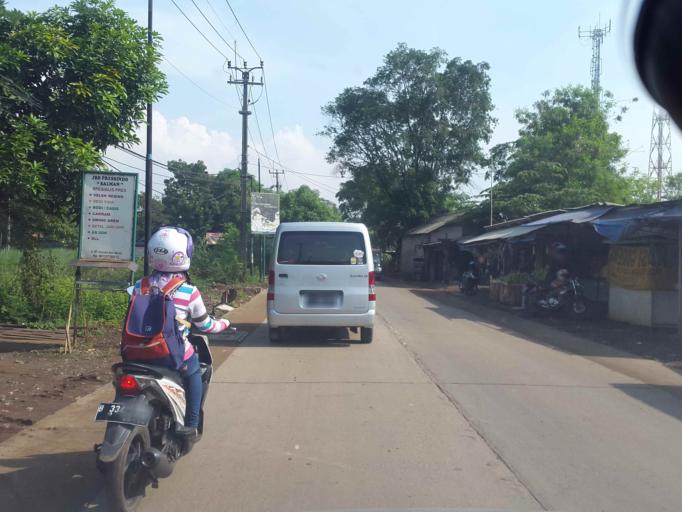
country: ID
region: West Java
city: Cileungsir
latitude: -6.3384
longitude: 107.0402
